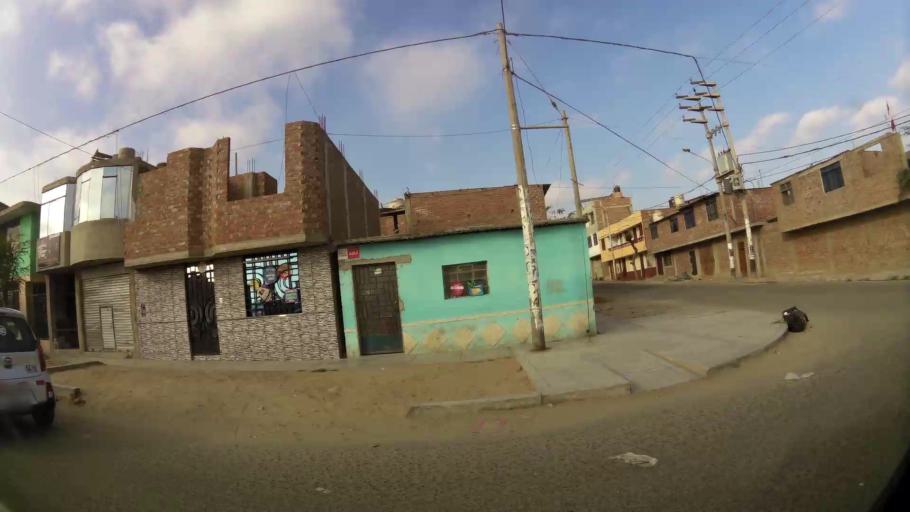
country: PE
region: La Libertad
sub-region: Provincia de Trujillo
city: La Esperanza
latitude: -8.0820
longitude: -79.0361
